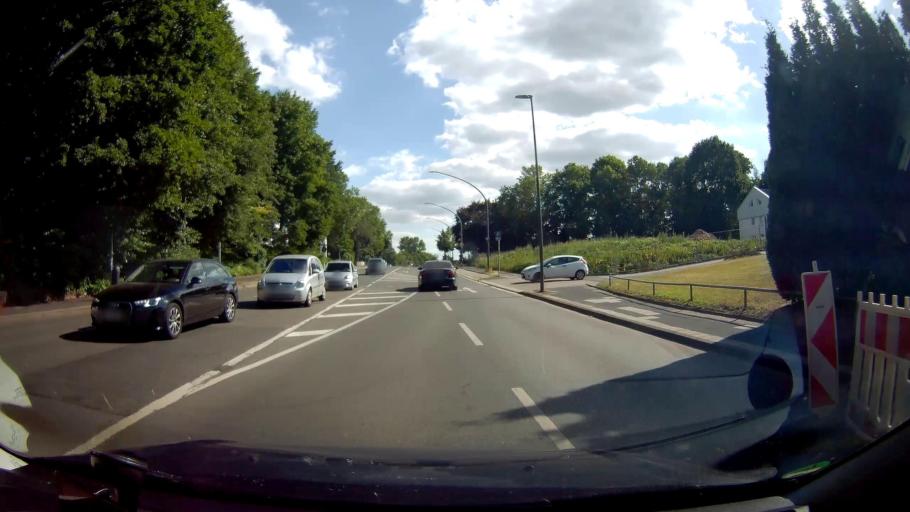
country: DE
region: North Rhine-Westphalia
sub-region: Regierungsbezirk Dusseldorf
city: Essen
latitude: 51.4881
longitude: 6.9803
